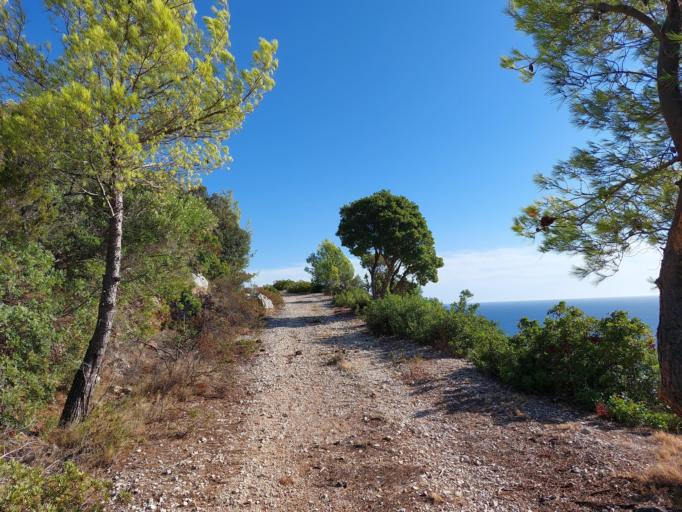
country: HR
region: Dubrovacko-Neretvanska
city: Smokvica
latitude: 42.7283
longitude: 16.8401
